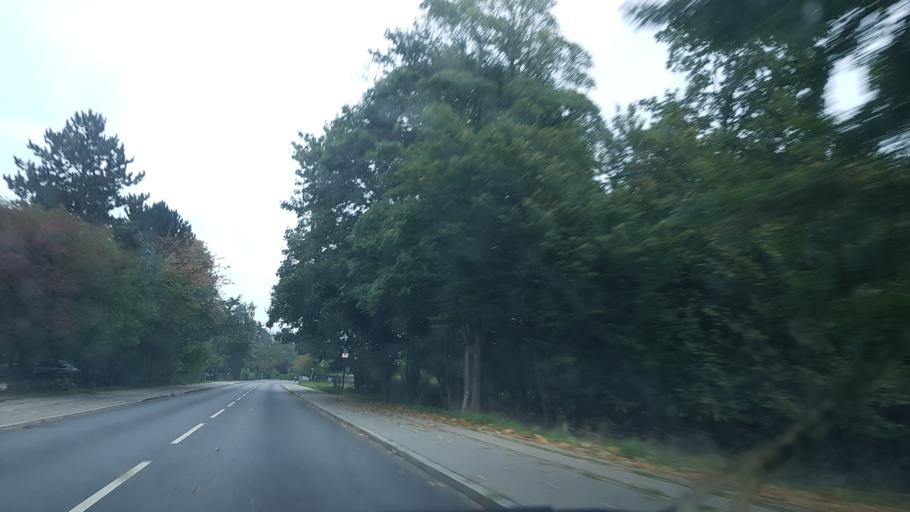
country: DK
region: Capital Region
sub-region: Rudersdal Kommune
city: Trorod
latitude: 55.8368
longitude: 12.5340
